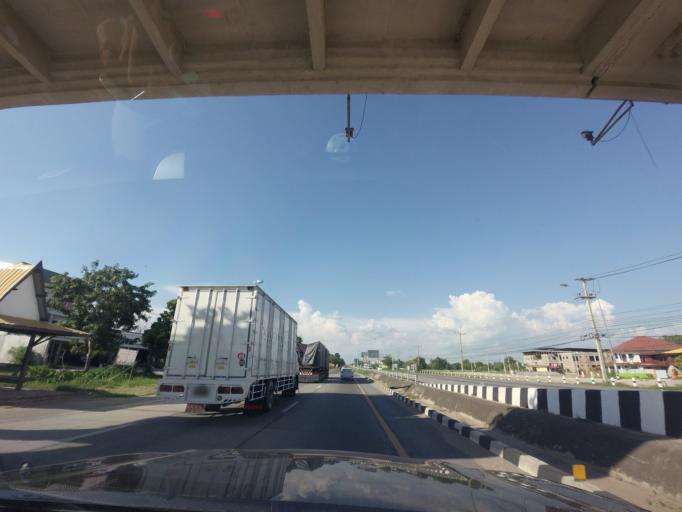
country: TH
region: Khon Kaen
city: Non Sila
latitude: 15.9669
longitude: 102.6916
